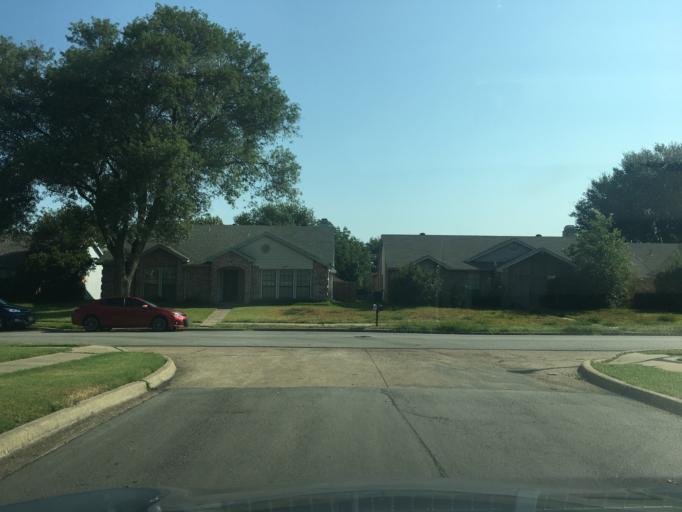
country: US
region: Texas
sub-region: Dallas County
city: Garland
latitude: 32.9438
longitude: -96.6249
